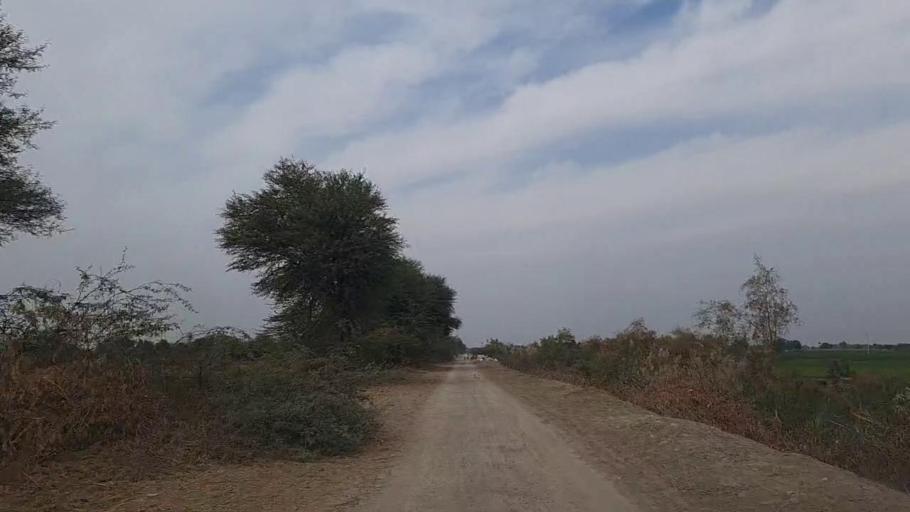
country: PK
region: Sindh
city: Daur
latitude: 26.4347
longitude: 68.4641
